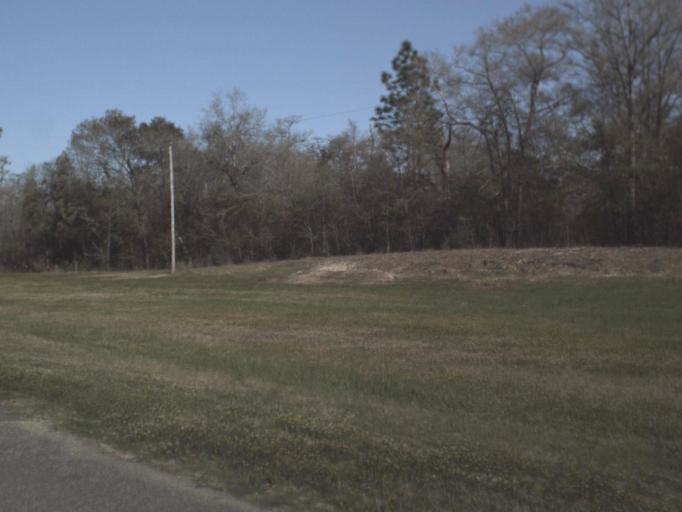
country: US
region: Florida
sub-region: Walton County
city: DeFuniak Springs
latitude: 30.7398
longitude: -85.9070
